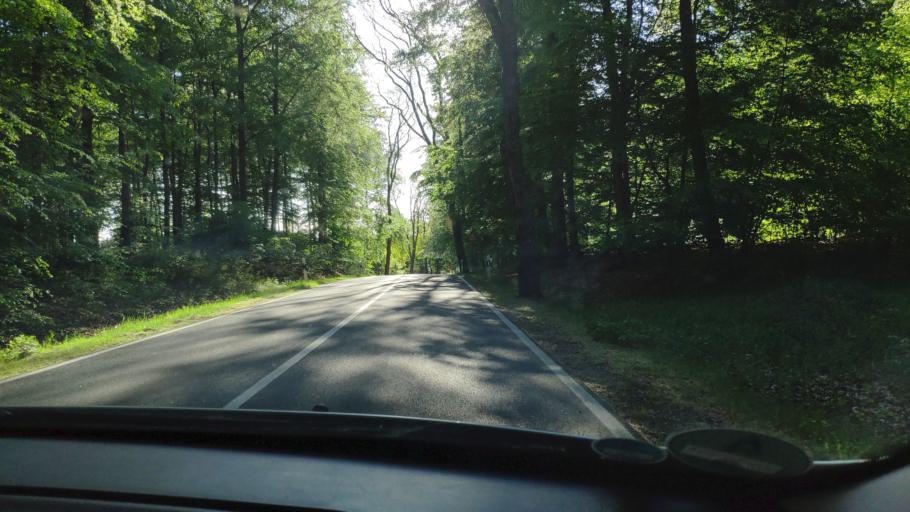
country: DE
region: Mecklenburg-Vorpommern
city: Wesenberg
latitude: 53.3211
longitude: 12.9536
